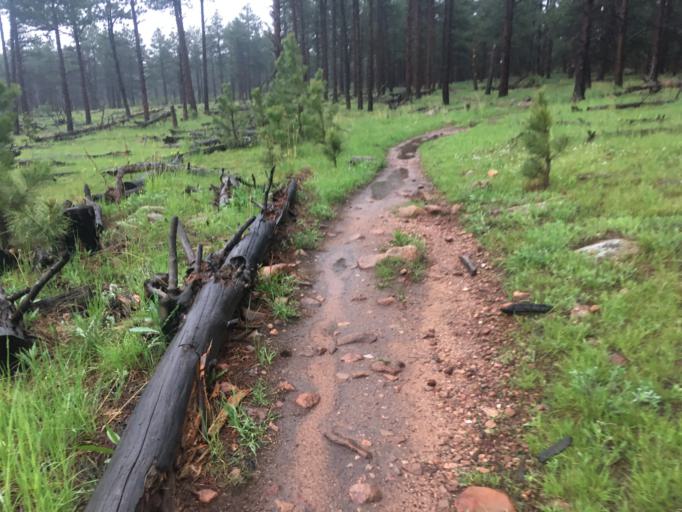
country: US
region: Colorado
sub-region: Boulder County
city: Boulder
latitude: 39.9190
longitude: -105.2678
